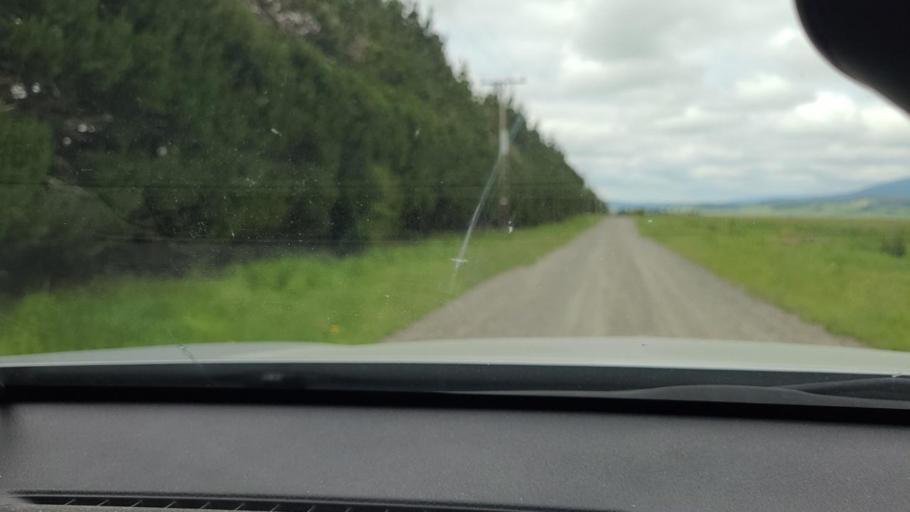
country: NZ
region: Southland
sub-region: Southland District
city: Riverton
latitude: -46.0570
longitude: 167.9477
